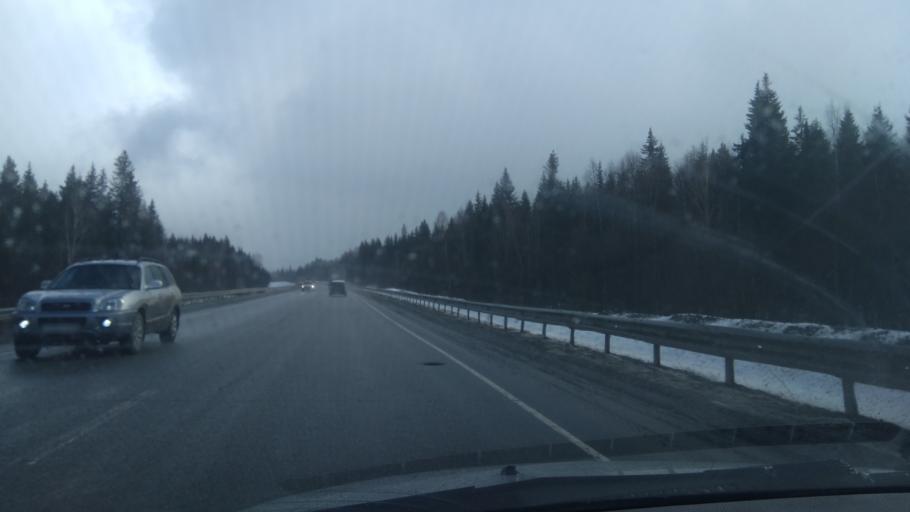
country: RU
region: Sverdlovsk
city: Arti
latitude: 56.7883
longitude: 58.5076
